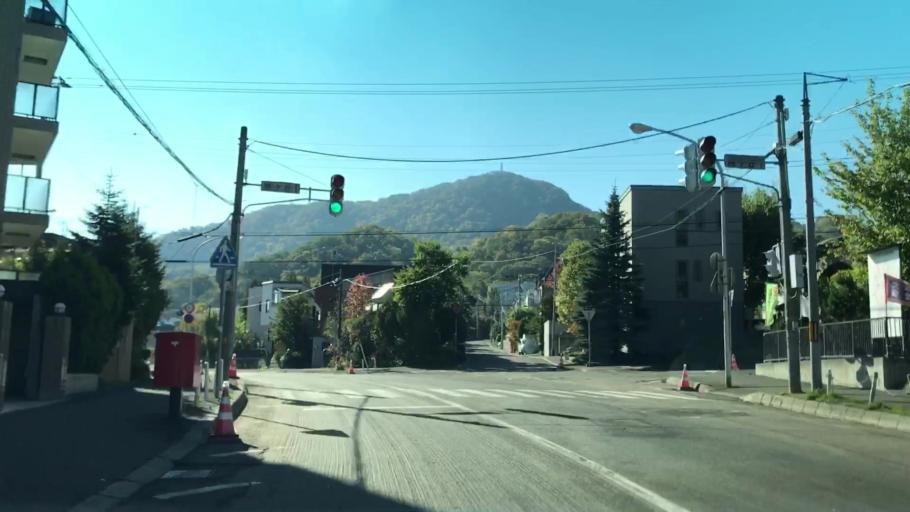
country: JP
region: Hokkaido
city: Sapporo
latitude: 43.0409
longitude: 141.3201
